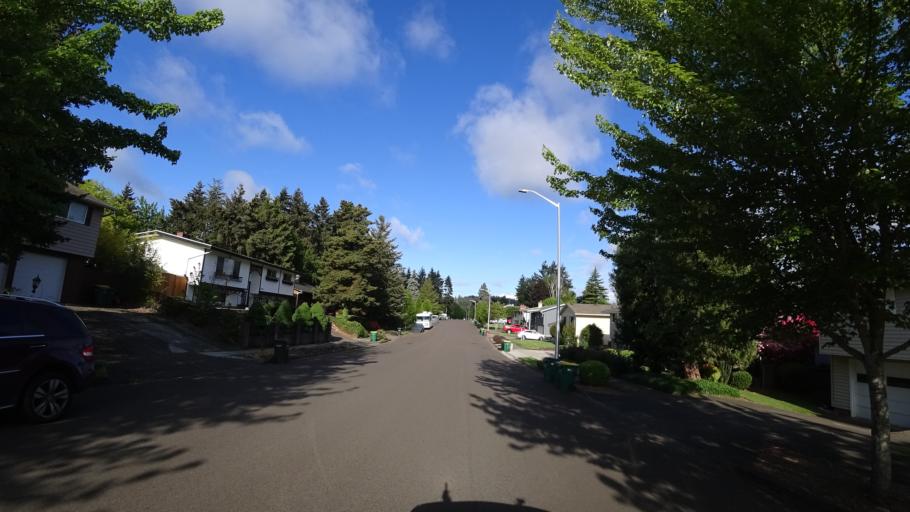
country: US
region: Oregon
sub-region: Washington County
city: Beaverton
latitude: 45.4721
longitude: -122.8219
